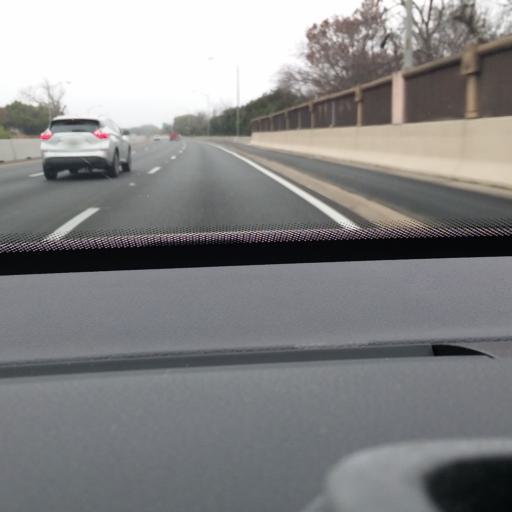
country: US
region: Texas
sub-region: Dallas County
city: University Park
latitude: 32.8561
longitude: -96.7912
